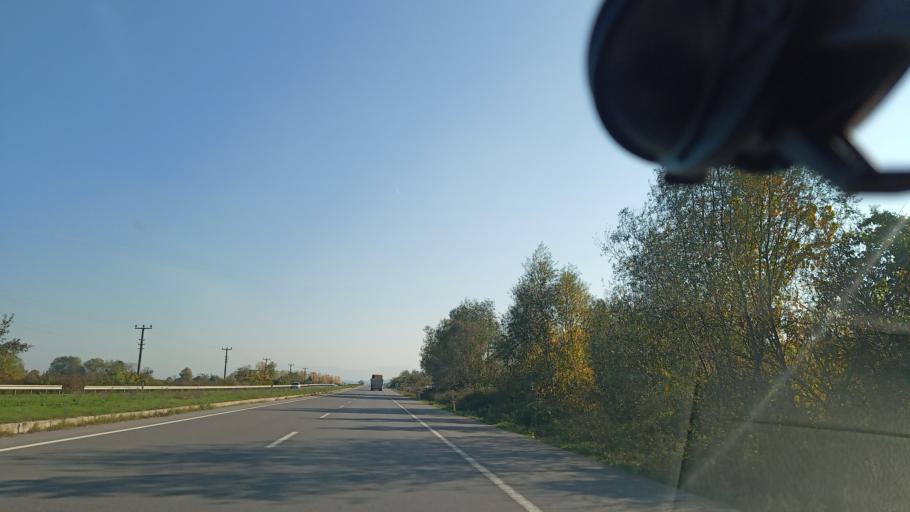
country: TR
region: Sakarya
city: Karasu
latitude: 41.0748
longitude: 30.7845
